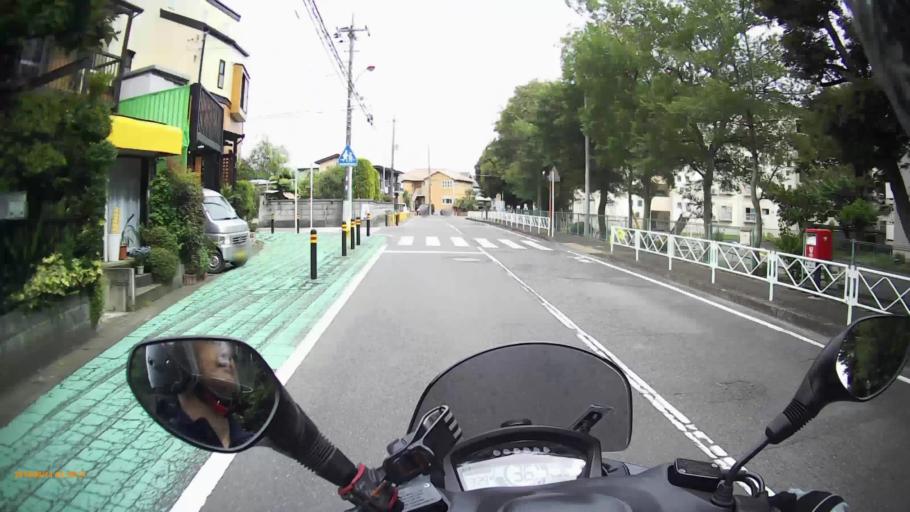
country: JP
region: Kanagawa
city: Minami-rinkan
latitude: 35.4150
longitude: 139.4489
